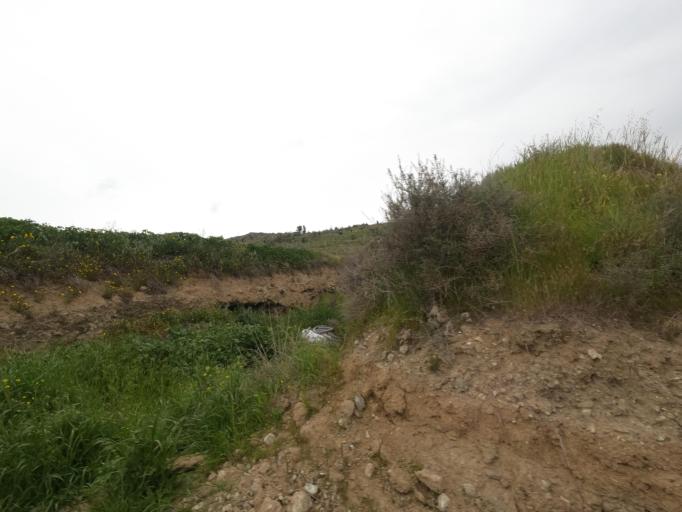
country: CY
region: Lefkosia
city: Astromeritis
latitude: 35.0900
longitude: 32.9518
